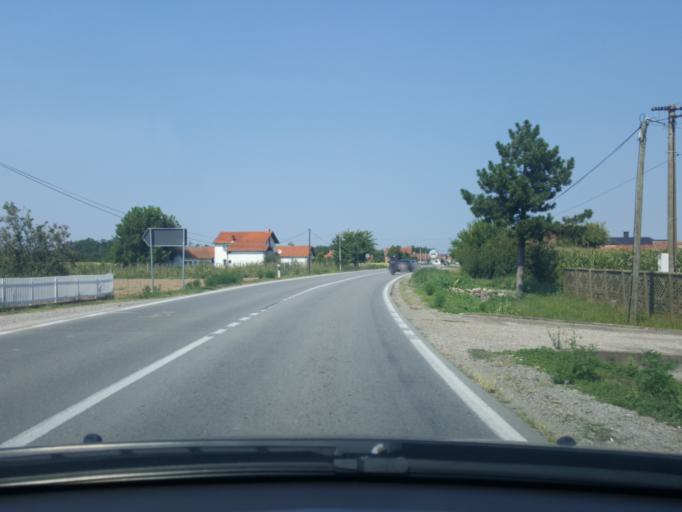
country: RS
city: Dublje
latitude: 44.7498
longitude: 19.5272
